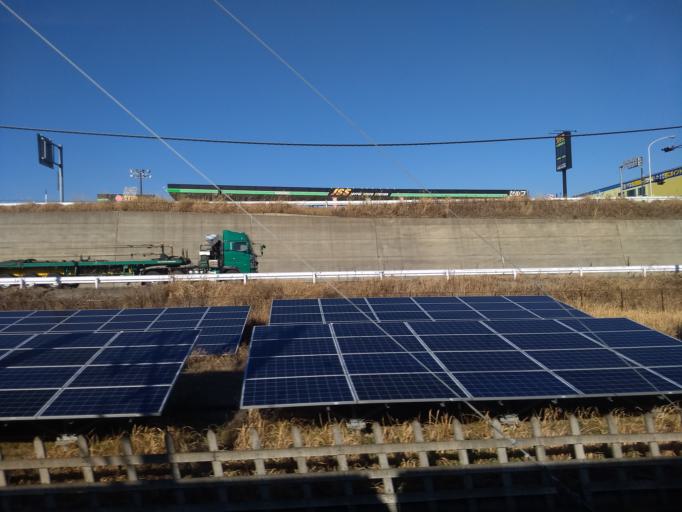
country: JP
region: Chiba
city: Shiroi
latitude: 35.8051
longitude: 140.1594
